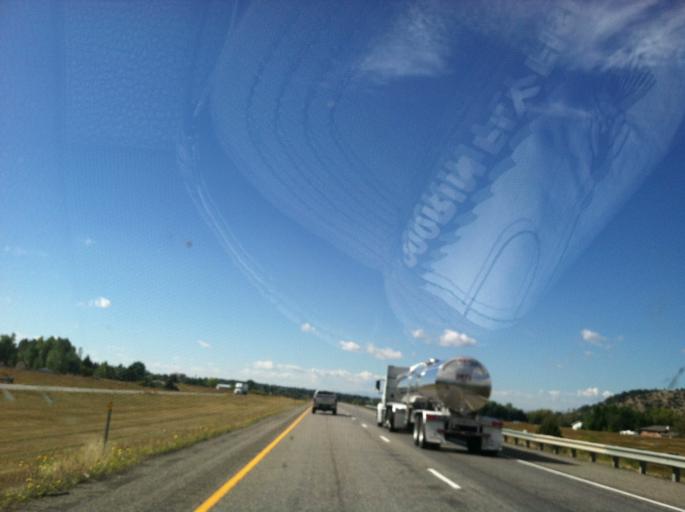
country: US
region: Montana
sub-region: Gallatin County
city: Bozeman
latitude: 45.6674
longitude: -110.9844
